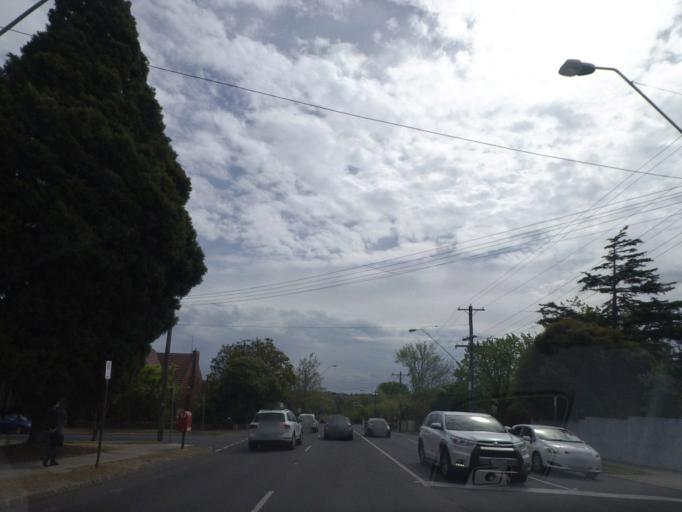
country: AU
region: Victoria
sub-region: Boroondara
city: Ashburton
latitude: -37.8624
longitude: 145.0709
